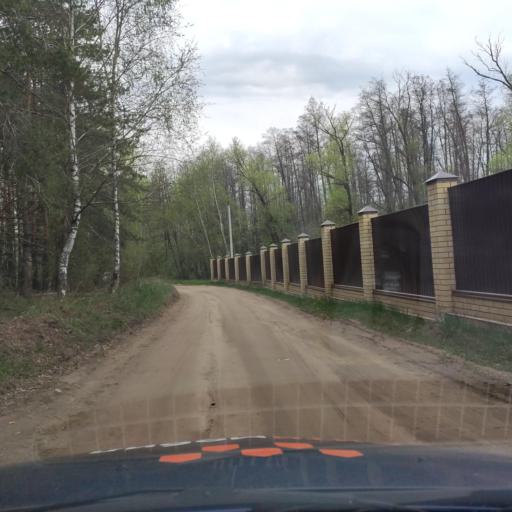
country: RU
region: Voronezj
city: Podgornoye
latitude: 51.8681
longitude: 39.1689
